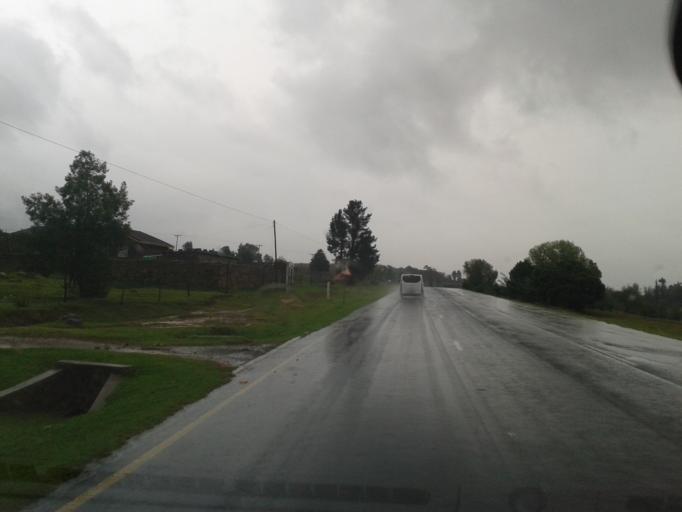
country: LS
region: Maseru
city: Nako
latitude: -29.6406
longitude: 27.4767
